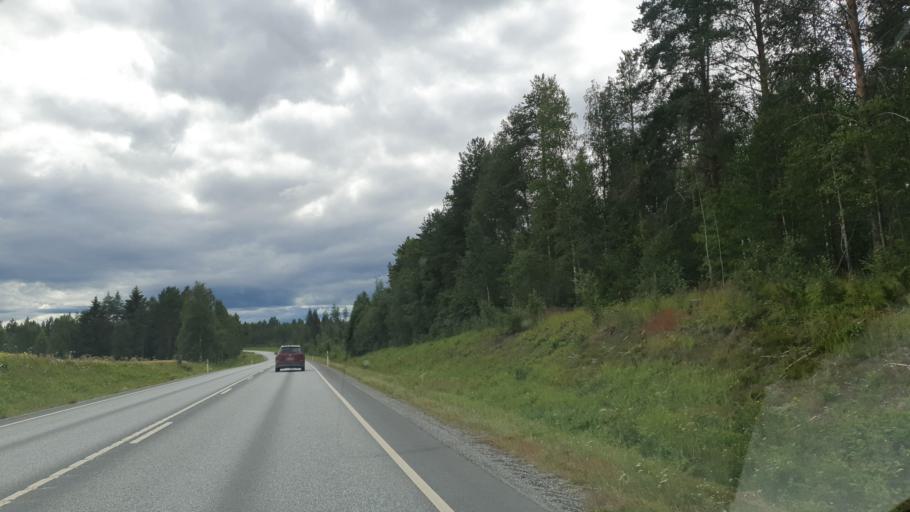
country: FI
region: Northern Savo
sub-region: Ylae-Savo
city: Sonkajaervi
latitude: 63.8410
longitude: 27.4305
